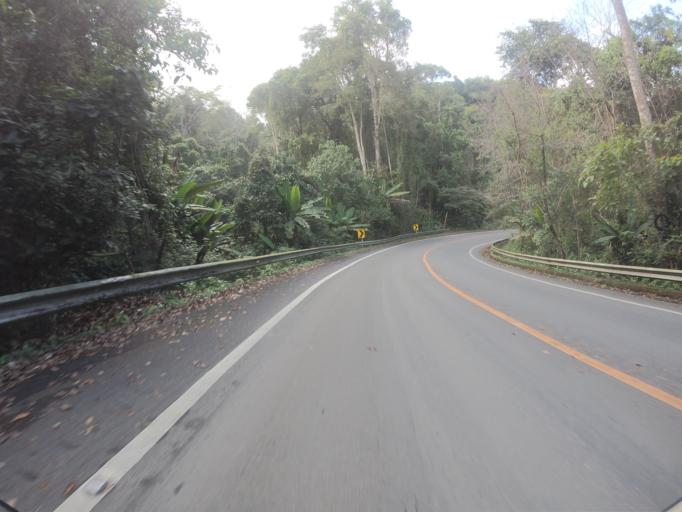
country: TH
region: Chiang Mai
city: Chiang Mai
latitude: 18.8018
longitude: 98.9084
